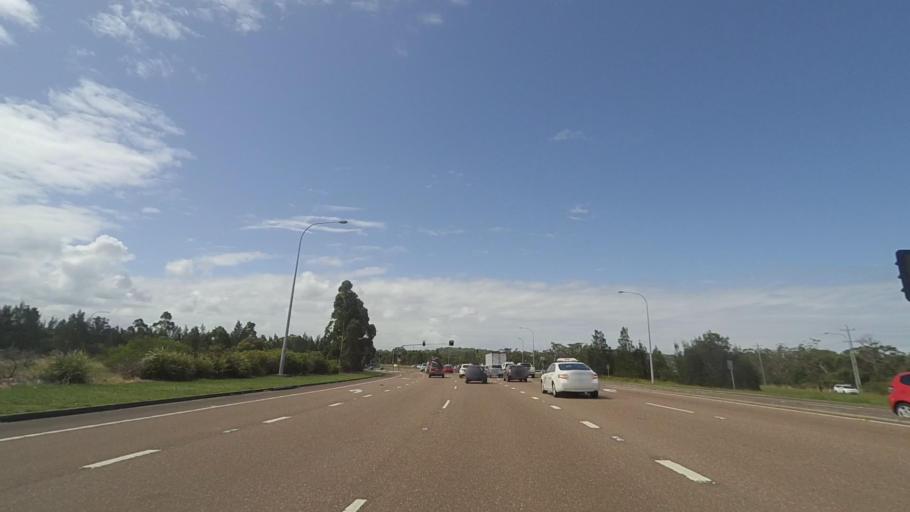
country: AU
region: New South Wales
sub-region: Lake Macquarie Shire
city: Windale
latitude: -32.9931
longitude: 151.6886
